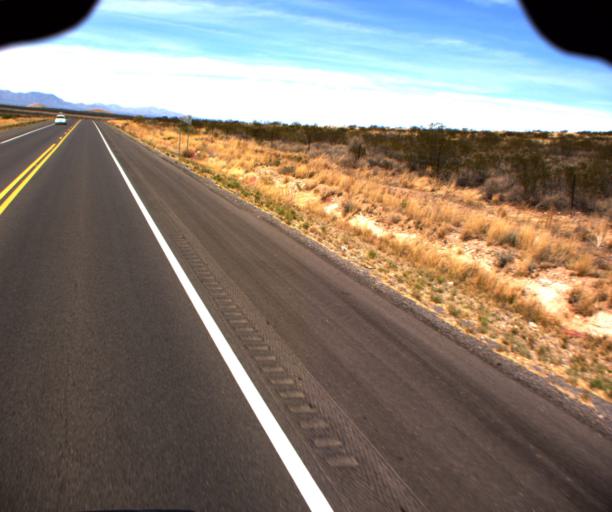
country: US
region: Arizona
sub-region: Cochise County
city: Willcox
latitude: 31.9014
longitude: -109.7106
